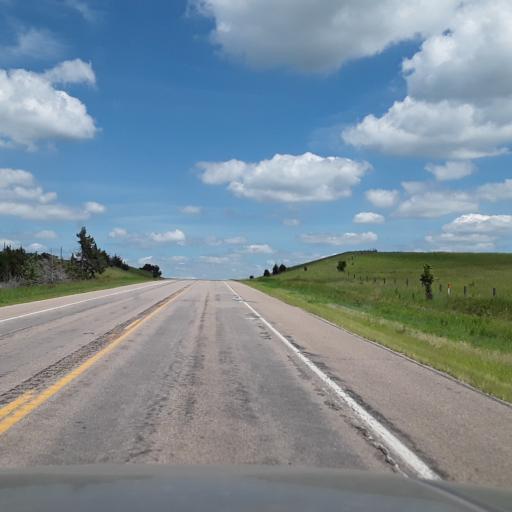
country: US
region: Nebraska
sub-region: Nance County
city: Genoa
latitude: 41.4720
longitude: -97.7034
